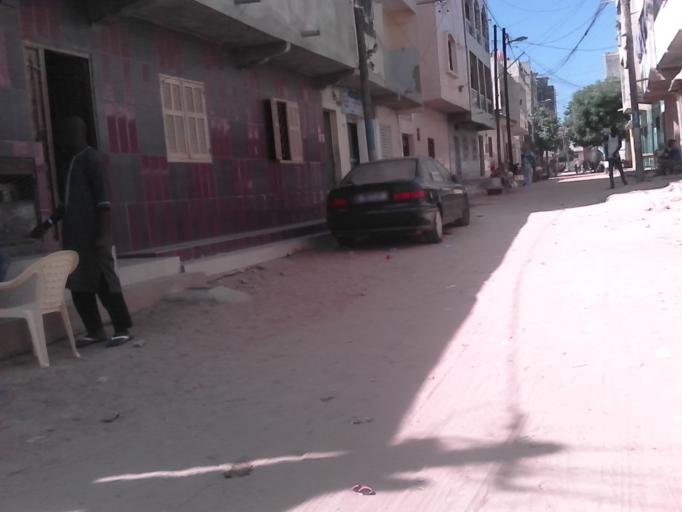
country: SN
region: Dakar
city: Grand Dakar
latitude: 14.7066
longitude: -17.4528
